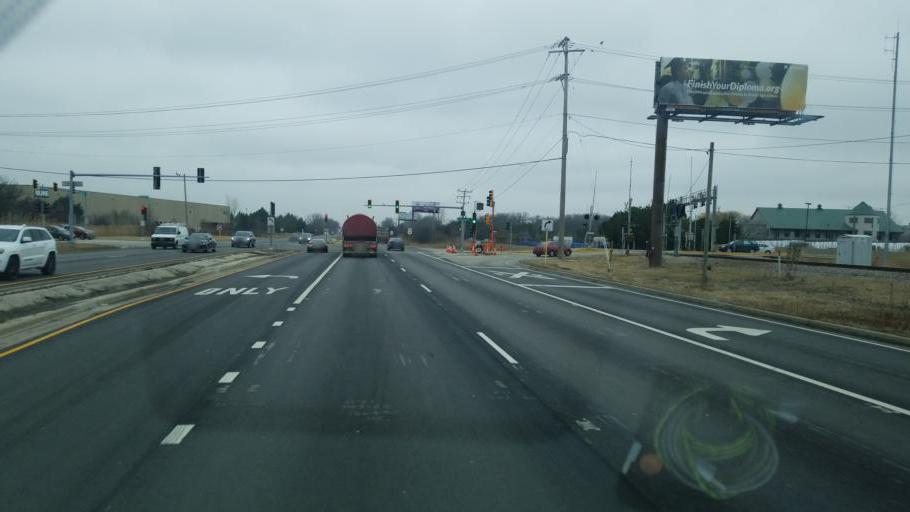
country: US
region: Illinois
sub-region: Lake County
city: Park City
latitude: 42.3188
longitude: -87.8800
